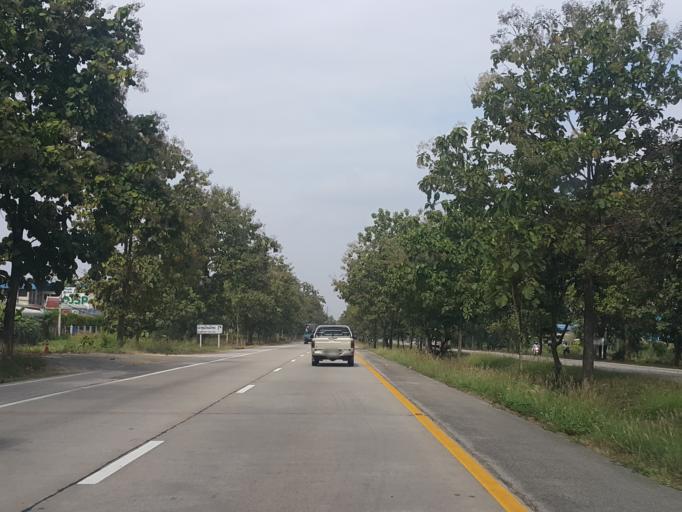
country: TH
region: Lamphun
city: Lamphun
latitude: 18.5308
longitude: 99.0787
